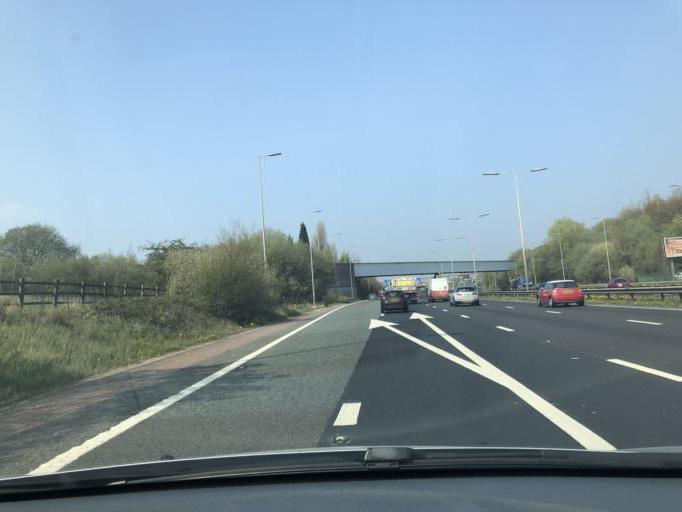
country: GB
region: England
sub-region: Borough of Tameside
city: Denton
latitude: 53.4509
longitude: -2.1356
